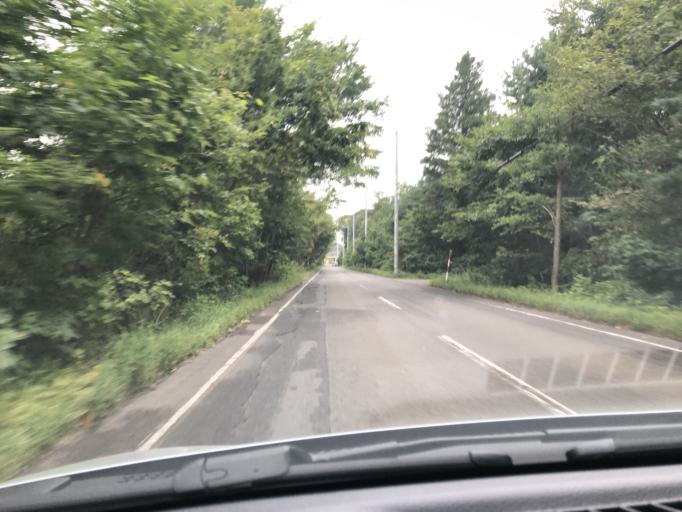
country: JP
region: Hokkaido
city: Chitose
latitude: 42.8709
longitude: 141.7187
